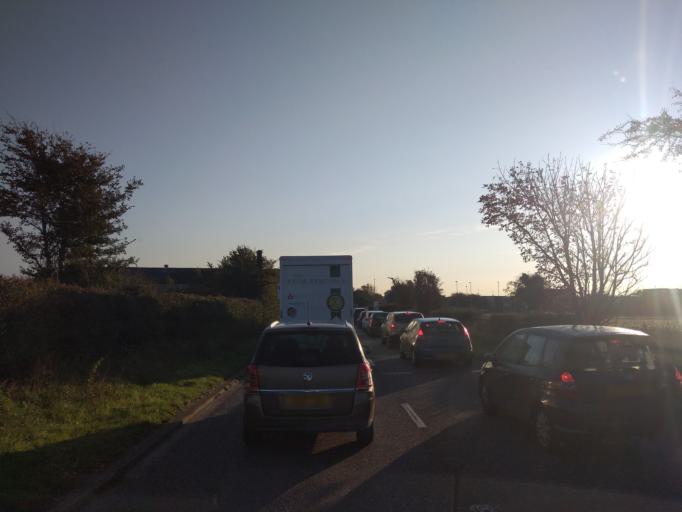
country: GB
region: England
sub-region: West Sussex
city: Goring-by-Sea
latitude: 50.8222
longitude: -0.4371
